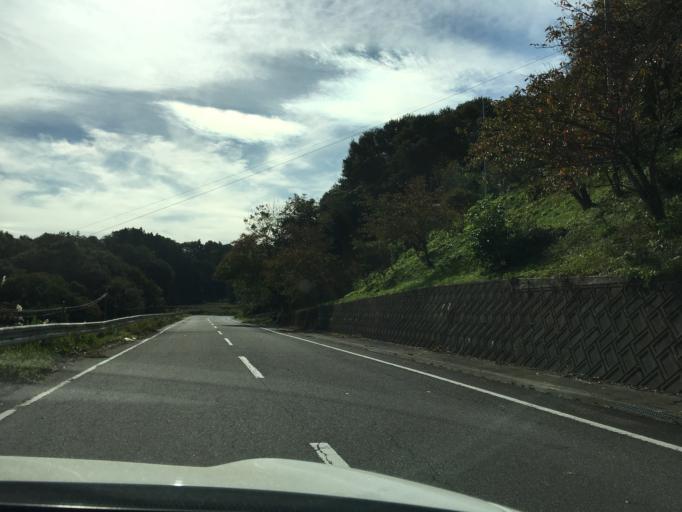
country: JP
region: Fukushima
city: Nihommatsu
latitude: 37.5287
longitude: 140.5055
